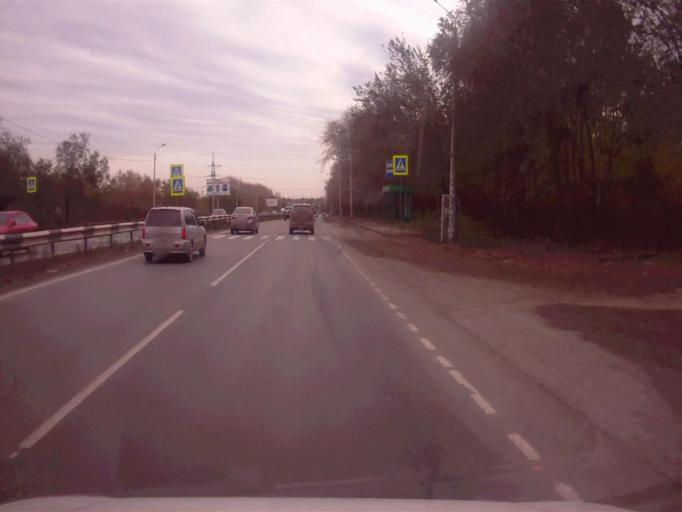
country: RU
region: Chelyabinsk
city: Novosineglazovskiy
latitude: 55.0521
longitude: 61.4112
